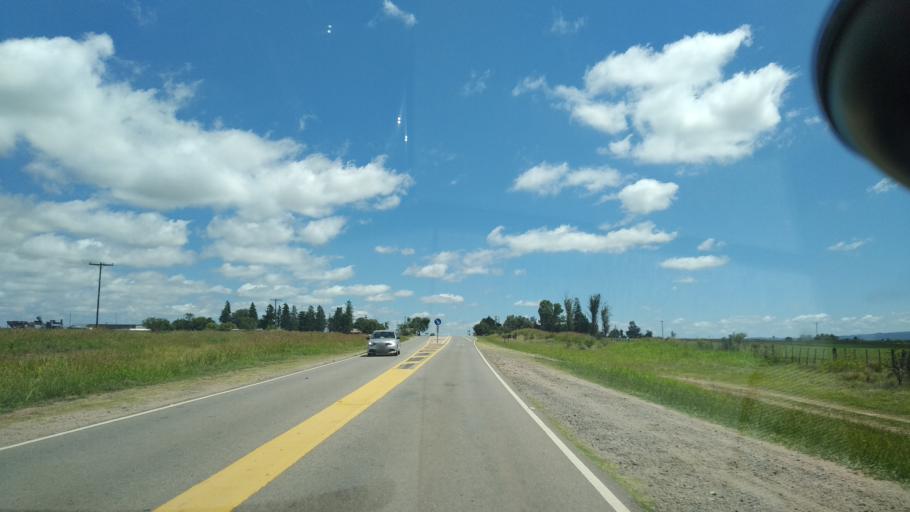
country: AR
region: Cordoba
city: Villa Cura Brochero
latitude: -31.6580
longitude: -65.0986
